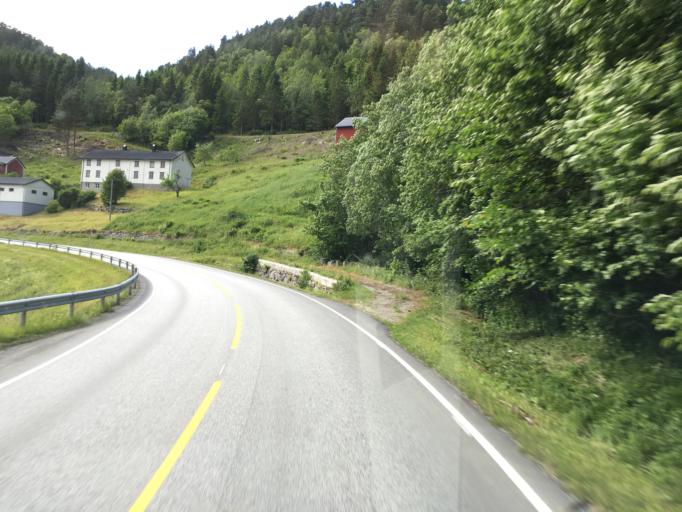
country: NO
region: More og Romsdal
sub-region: Tingvoll
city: Tingvoll
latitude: 62.9756
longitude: 8.0669
